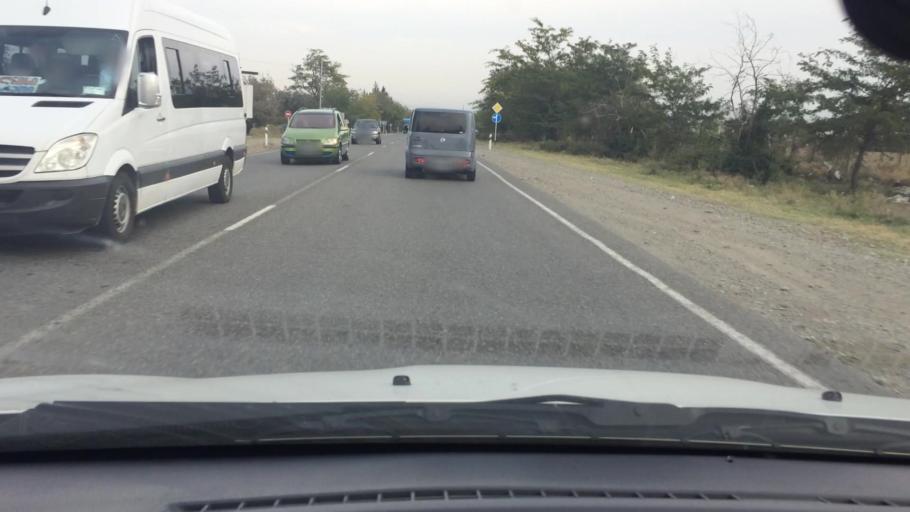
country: GE
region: T'bilisi
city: Tbilisi
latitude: 41.6428
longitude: 44.8553
